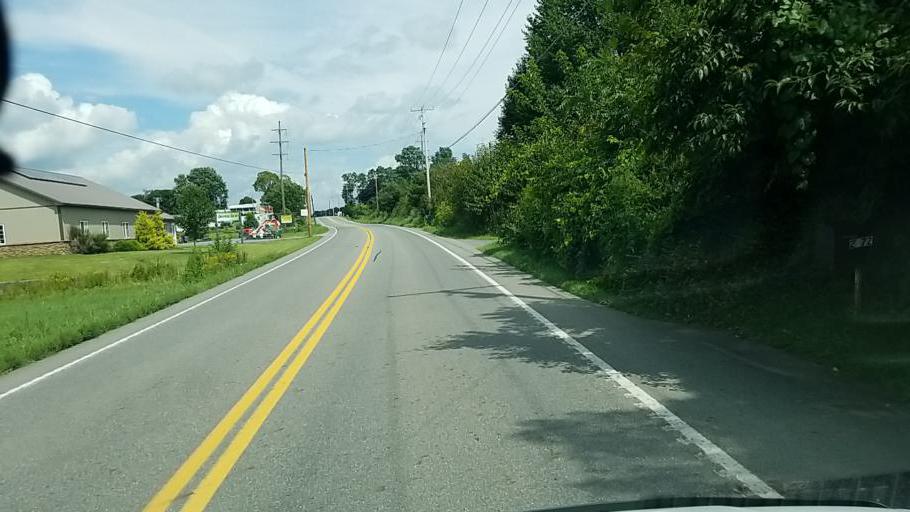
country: US
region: Pennsylvania
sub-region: Dauphin County
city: Elizabethville
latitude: 40.5827
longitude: -76.8673
